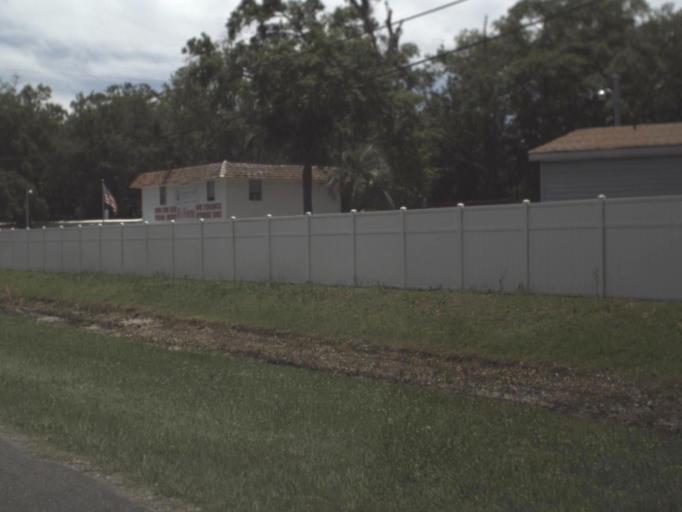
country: US
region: Florida
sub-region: Duval County
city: Jacksonville
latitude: 30.4081
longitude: -81.7453
